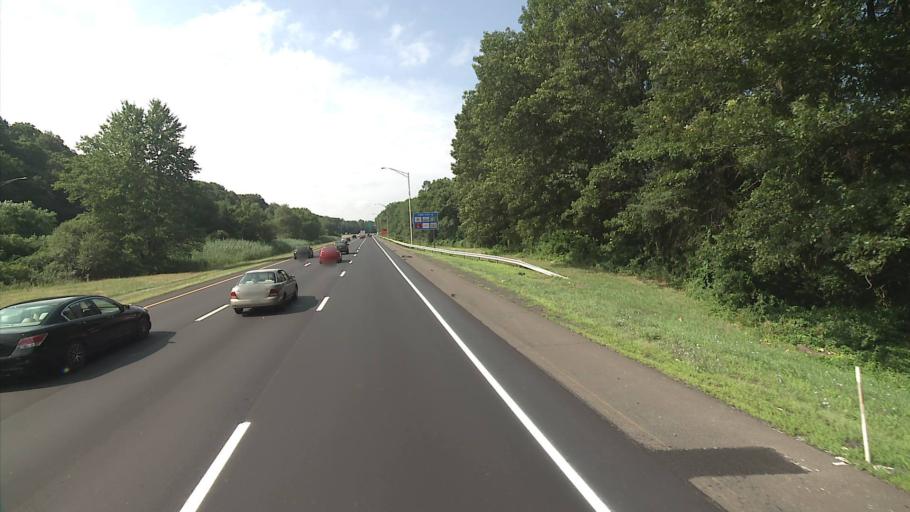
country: US
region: Connecticut
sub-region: New Haven County
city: North Haven
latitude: 41.4116
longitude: -72.8318
